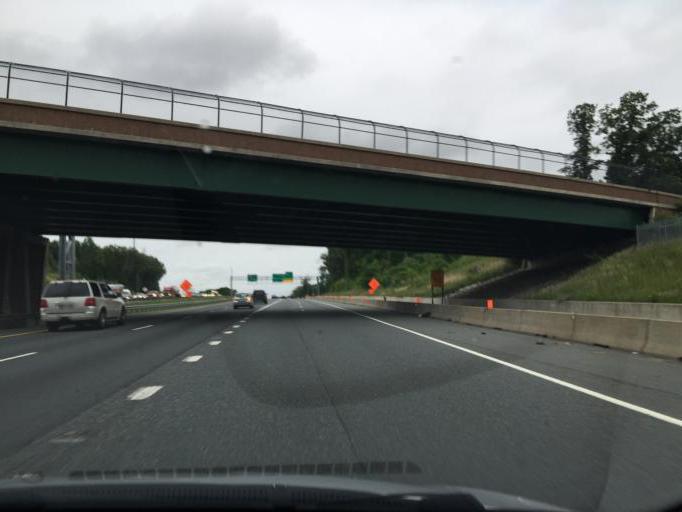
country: US
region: Maryland
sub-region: Baltimore County
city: Overlea
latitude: 39.3614
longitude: -76.5060
